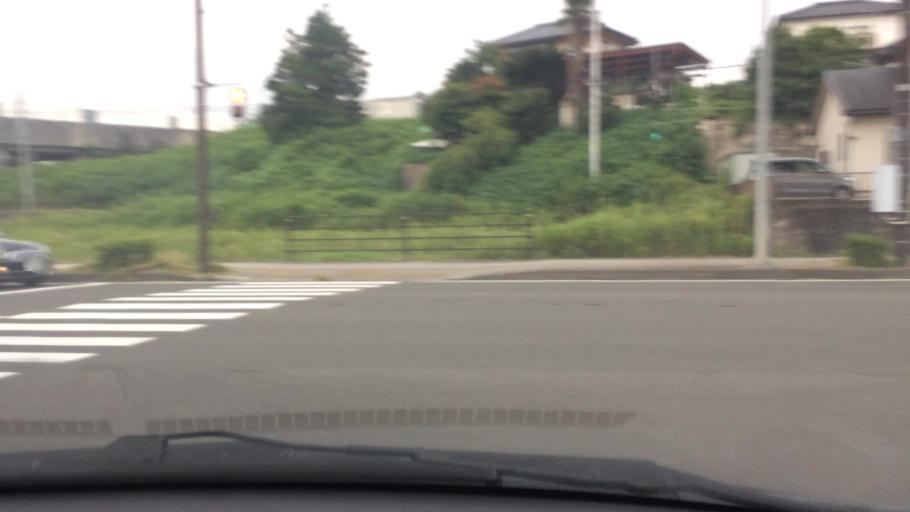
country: JP
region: Miyagi
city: Rifu
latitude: 38.3276
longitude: 140.9701
